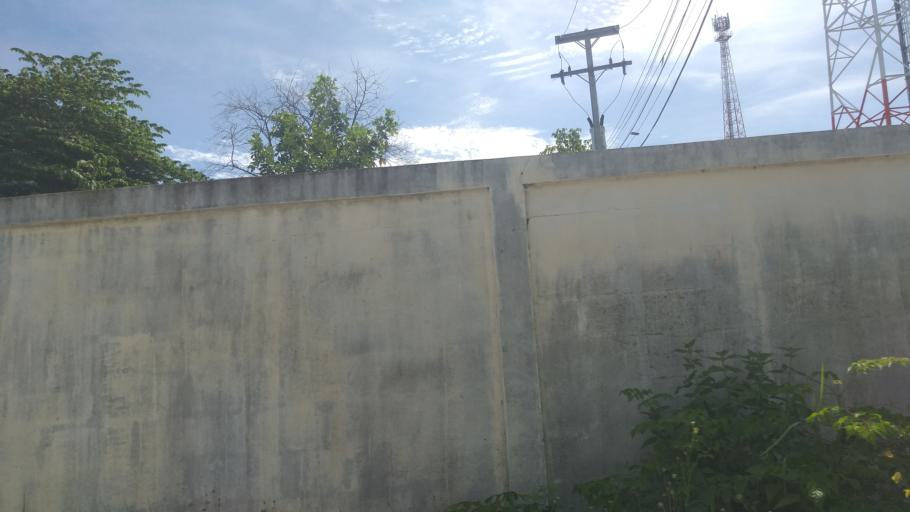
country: TH
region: Chaiyaphum
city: Ban Thaen
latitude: 16.4065
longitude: 102.3443
